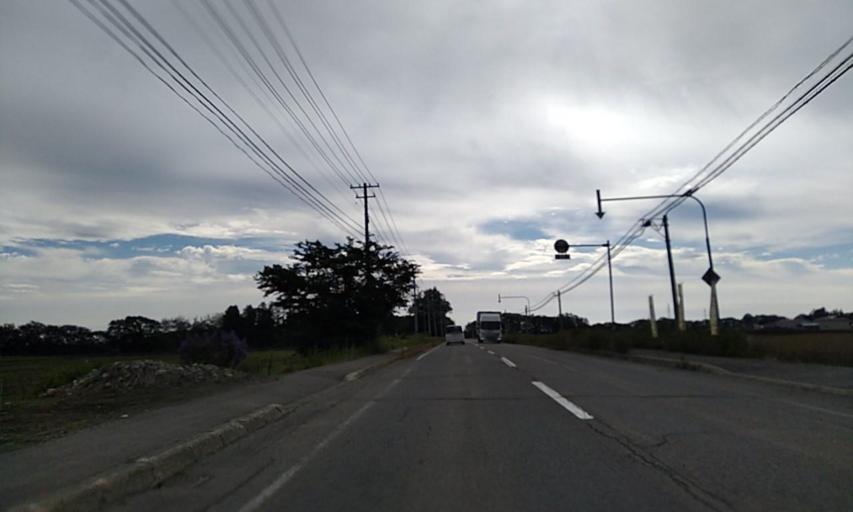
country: JP
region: Hokkaido
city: Obihiro
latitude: 42.8485
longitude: 143.1679
